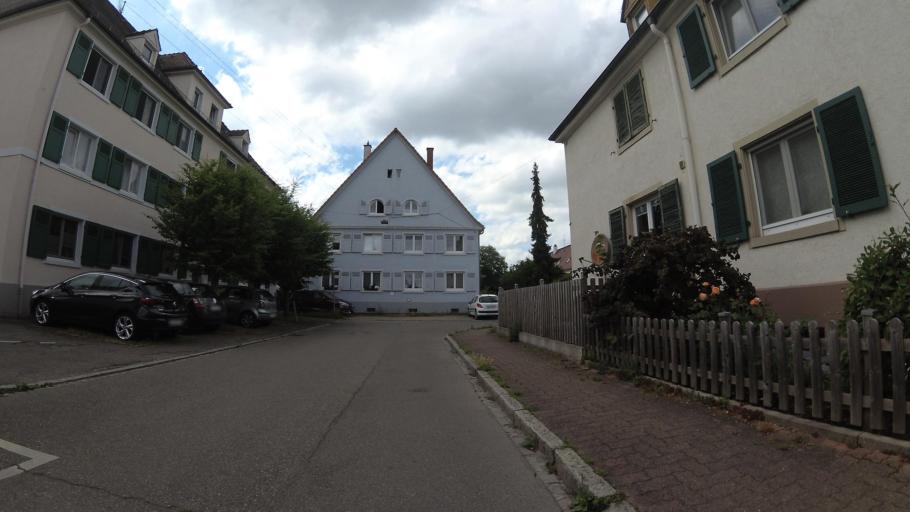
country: DE
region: Baden-Wuerttemberg
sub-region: Freiburg Region
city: Weil am Rhein
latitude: 47.5893
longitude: 7.6146
